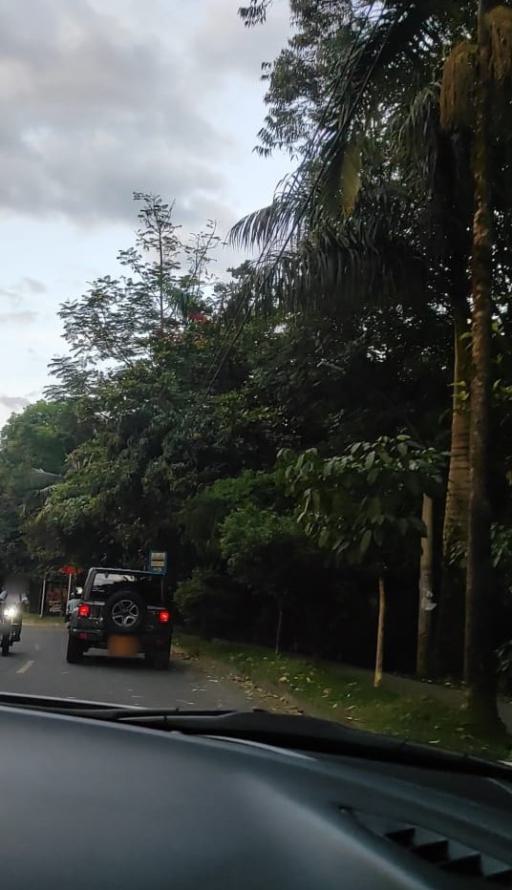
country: CO
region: Antioquia
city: Envigado
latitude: 6.1589
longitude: -75.5788
